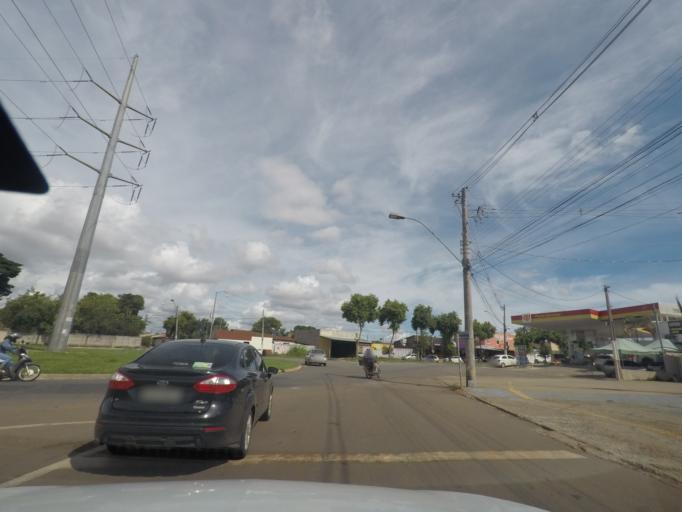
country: BR
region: Goias
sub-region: Goiania
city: Goiania
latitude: -16.7240
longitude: -49.3382
